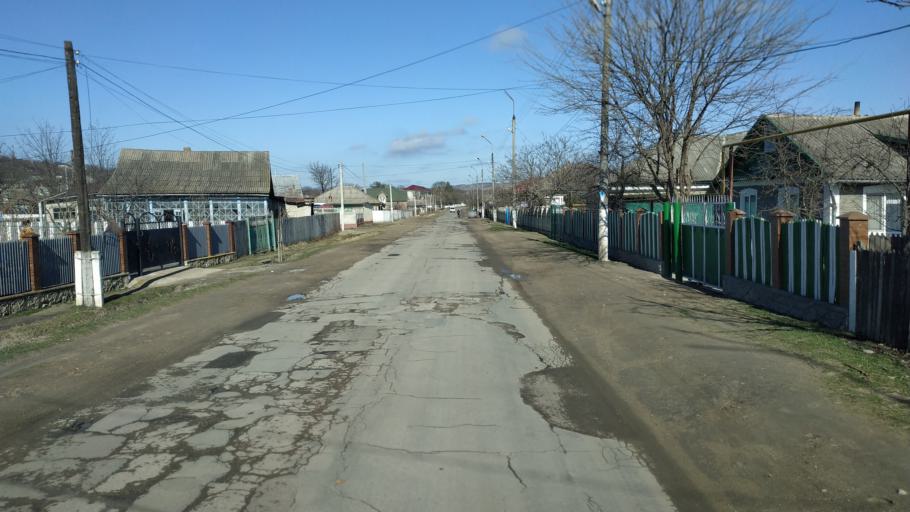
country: MD
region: Hincesti
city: Hincesti
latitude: 46.9571
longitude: 28.6055
